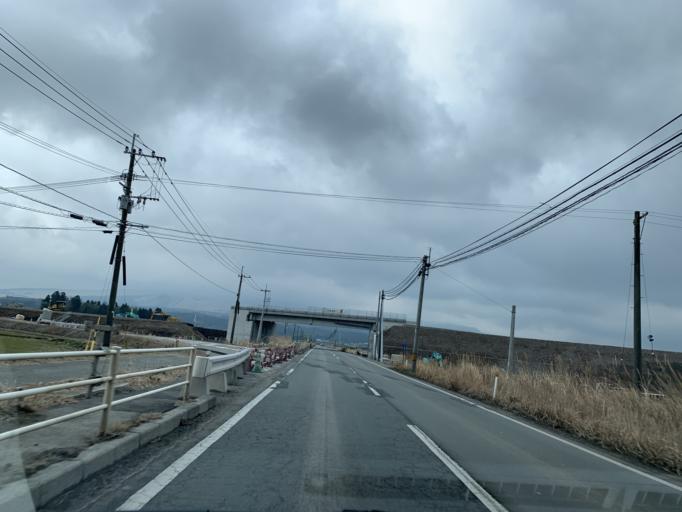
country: JP
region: Kumamoto
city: Aso
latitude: 32.9163
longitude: 130.9806
